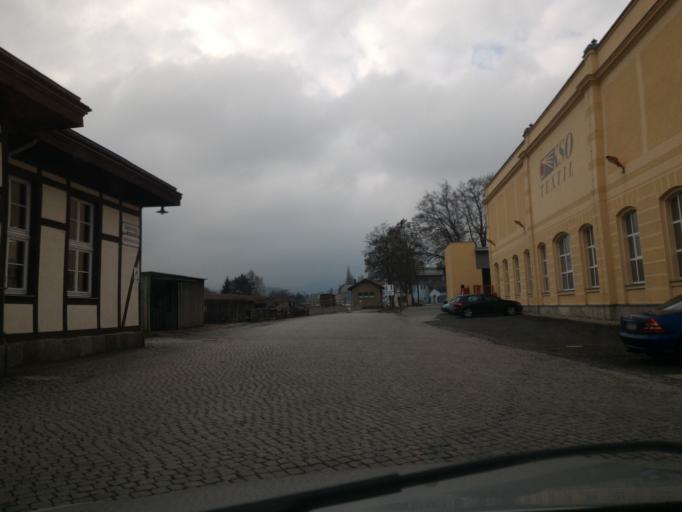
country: DE
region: Saxony
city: Zittau
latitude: 50.8909
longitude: 14.7918
